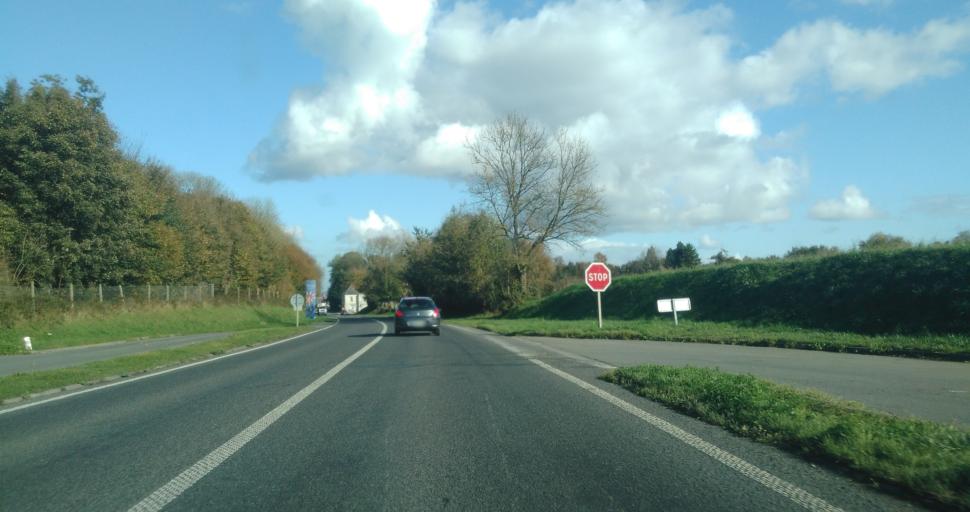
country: FR
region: Nord-Pas-de-Calais
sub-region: Departement du Pas-de-Calais
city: Beaumetz-les-Loges
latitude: 50.2366
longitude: 2.6499
